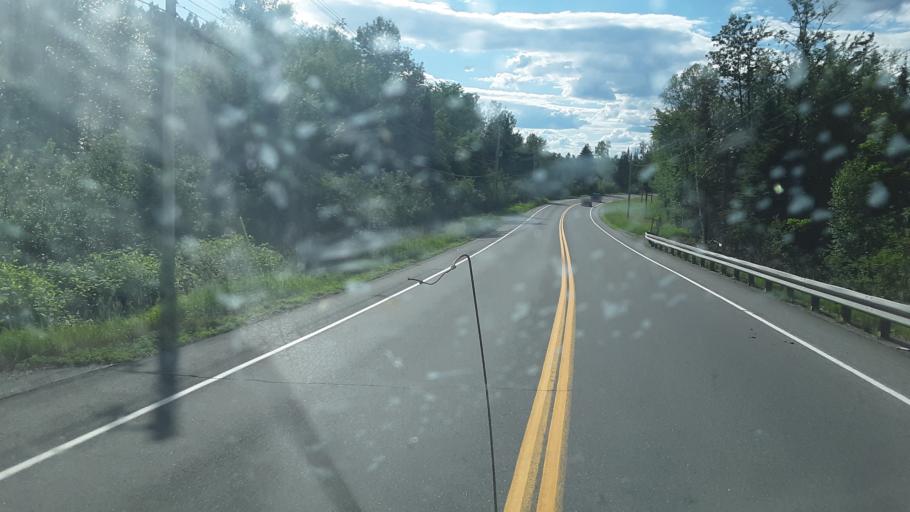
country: US
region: Maine
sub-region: Penobscot County
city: Patten
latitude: 45.8865
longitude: -68.4200
